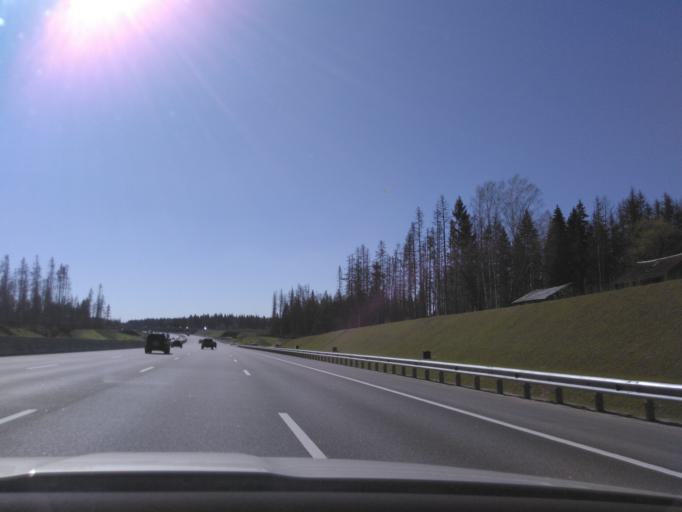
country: RU
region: Moskovskaya
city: Skhodnya
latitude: 55.9770
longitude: 37.3194
